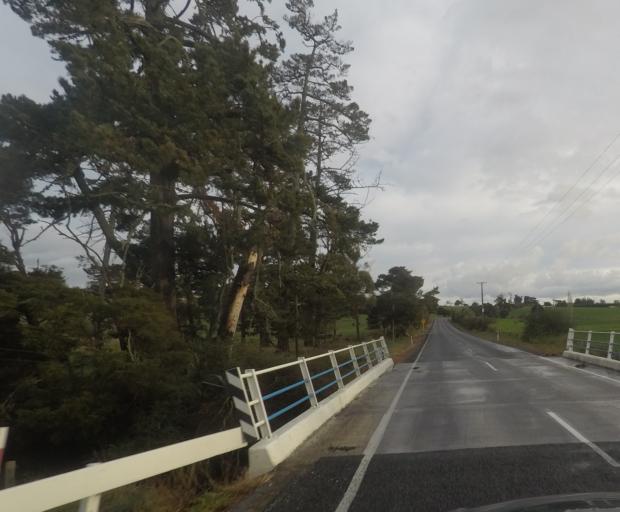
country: NZ
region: Auckland
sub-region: Auckland
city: Wellsford
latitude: -36.2131
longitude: 174.5860
